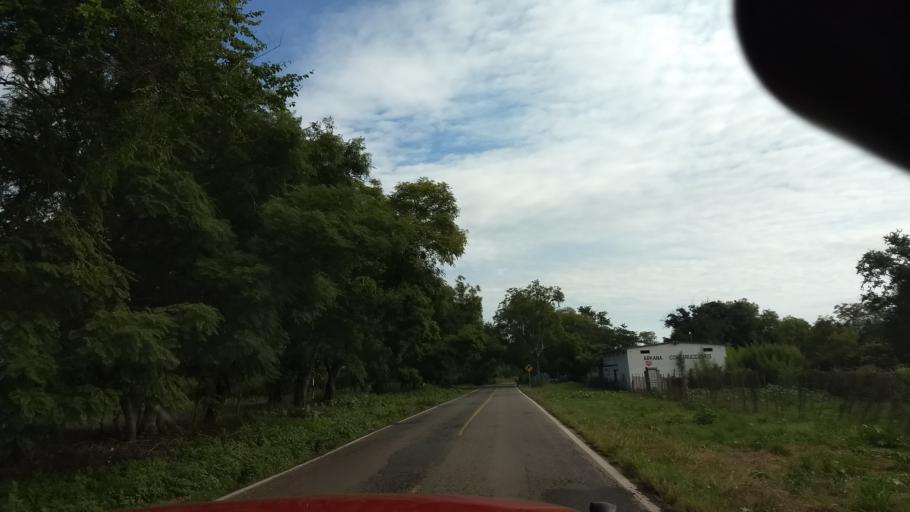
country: MX
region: Jalisco
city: Tuxpan
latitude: 19.5438
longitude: -103.4028
